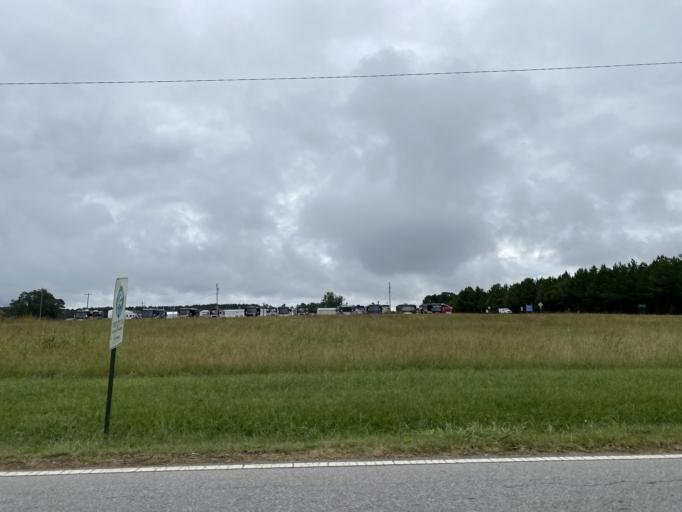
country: US
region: Alabama
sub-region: Franklin County
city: Red Bay
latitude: 34.4428
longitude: -88.1557
